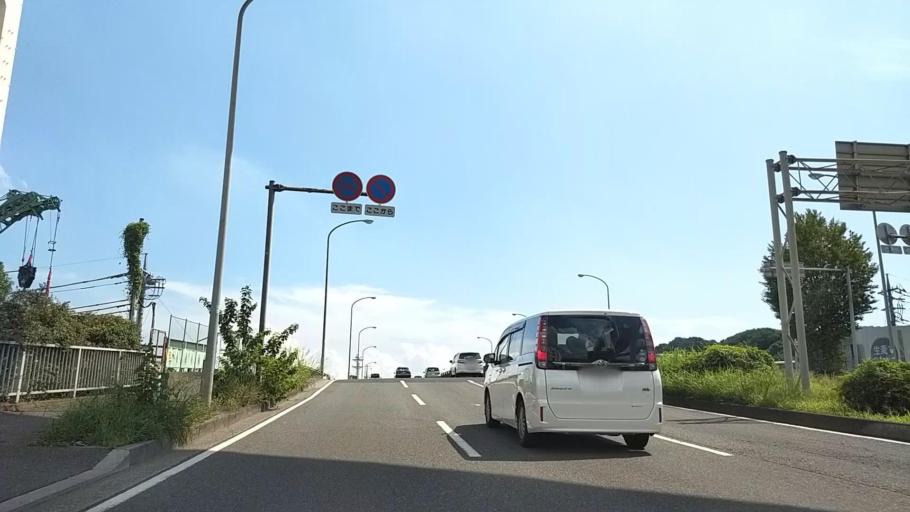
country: JP
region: Kanagawa
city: Yokohama
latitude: 35.5171
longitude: 139.5937
